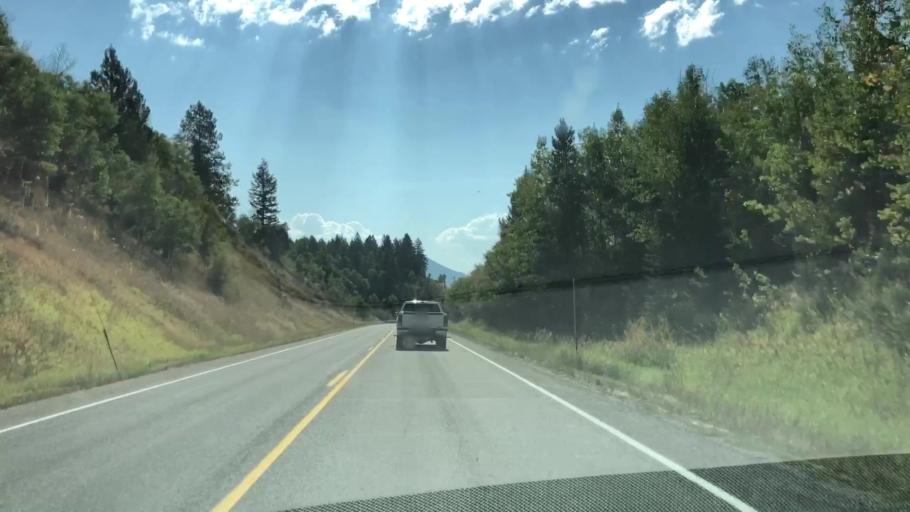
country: US
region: Wyoming
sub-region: Teton County
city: Hoback
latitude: 43.2311
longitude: -111.0912
